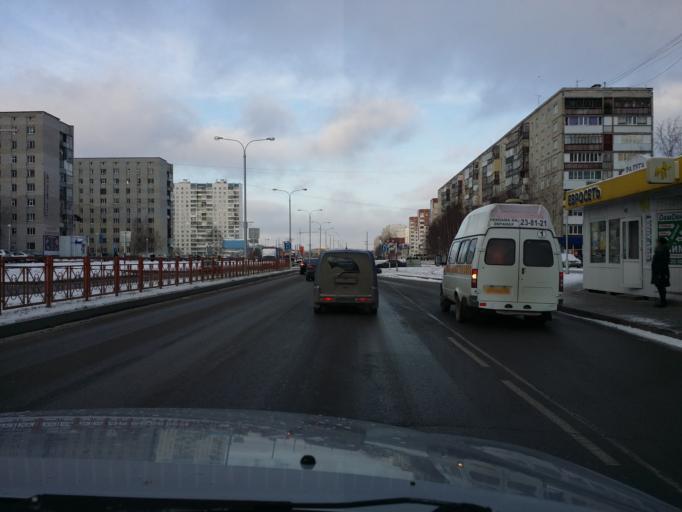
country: RU
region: Khanty-Mansiyskiy Avtonomnyy Okrug
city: Nizhnevartovsk
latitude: 60.9426
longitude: 76.5991
